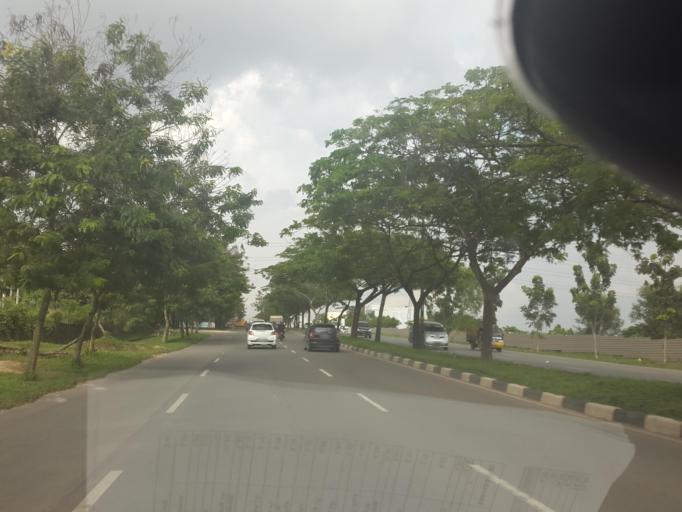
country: SG
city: Singapore
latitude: 1.1250
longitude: 104.0231
